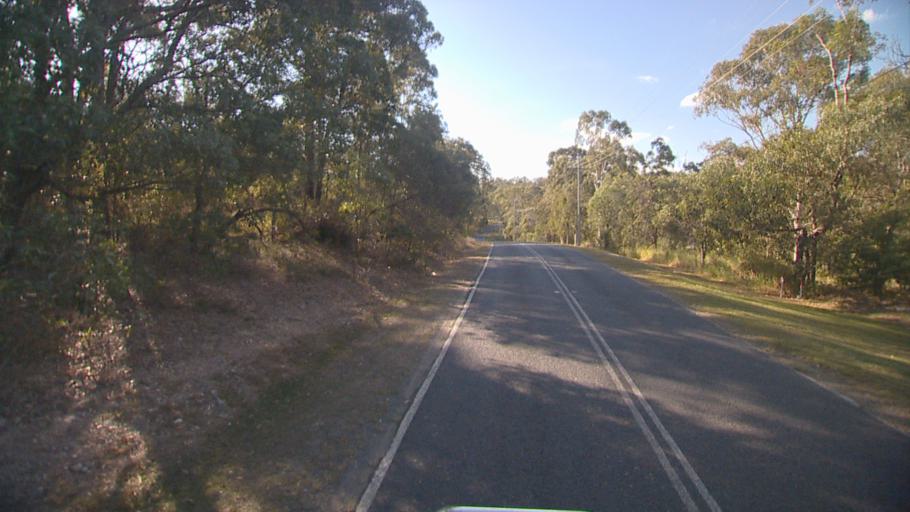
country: AU
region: Queensland
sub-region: Logan
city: Windaroo
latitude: -27.7307
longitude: 153.1715
